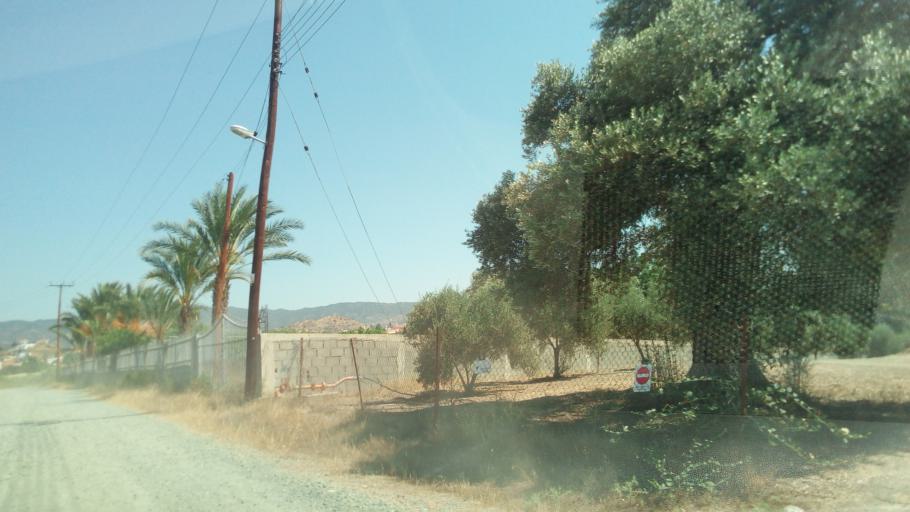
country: CY
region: Limassol
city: Pyrgos
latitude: 34.7328
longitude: 33.1816
